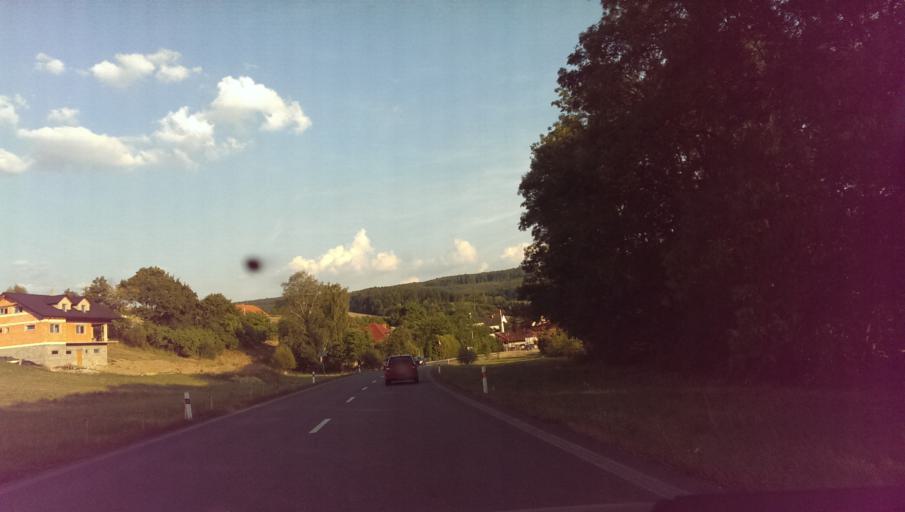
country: CZ
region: Zlin
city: Pozlovice
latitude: 49.1419
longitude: 17.8097
